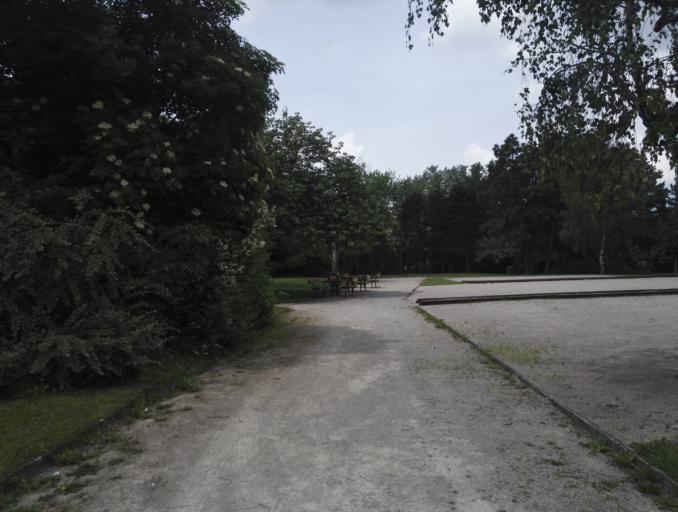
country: AT
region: Vienna
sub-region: Wien Stadt
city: Vienna
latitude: 48.2417
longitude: 16.4111
